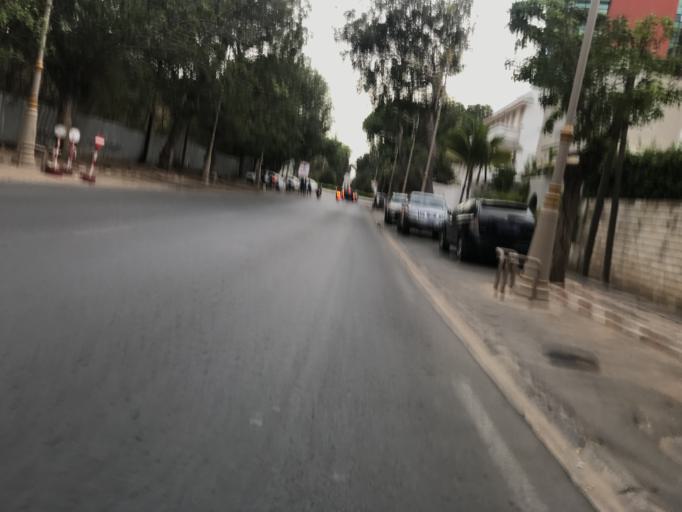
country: SN
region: Dakar
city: Dakar
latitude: 14.6627
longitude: -17.4361
